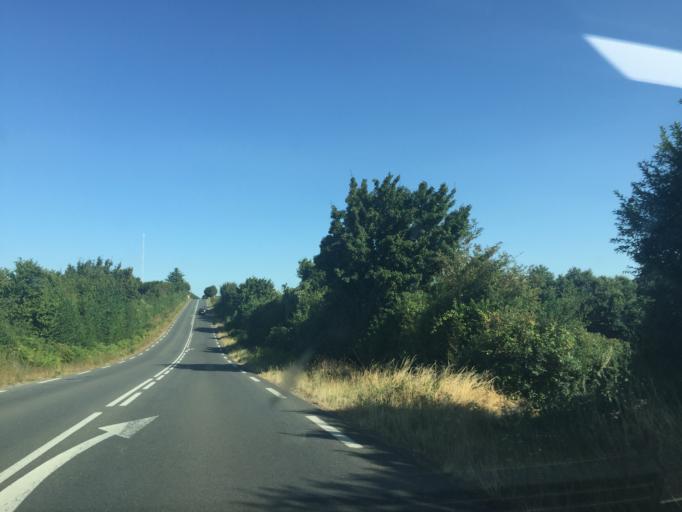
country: FR
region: Poitou-Charentes
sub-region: Departement des Deux-Sevres
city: Melle
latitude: 46.2016
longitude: -0.0868
